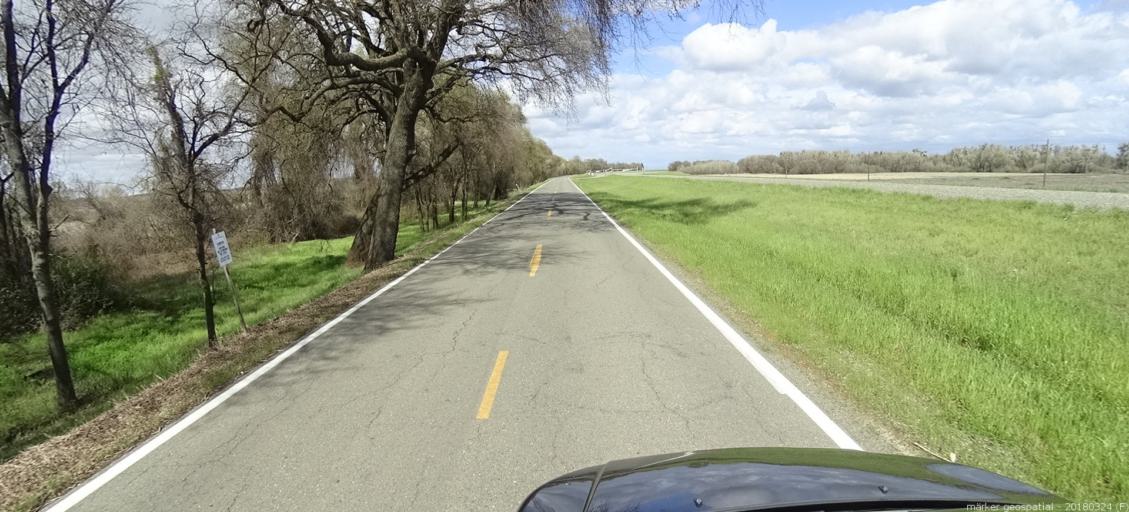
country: US
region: California
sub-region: Sacramento County
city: Elverta
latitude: 38.7363
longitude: -121.6015
